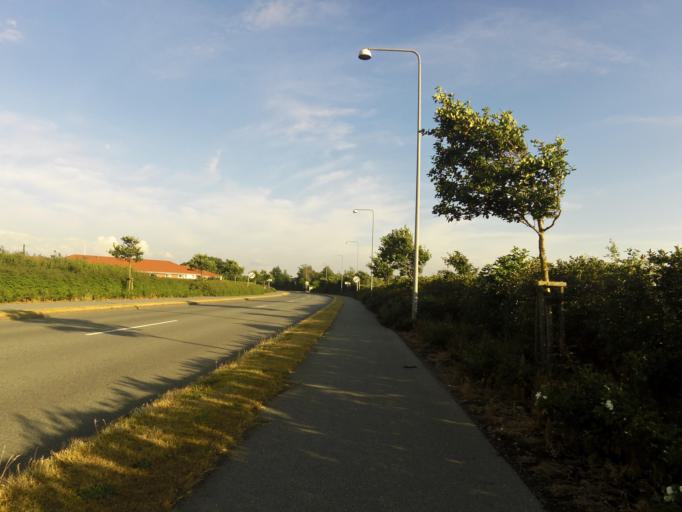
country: DK
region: South Denmark
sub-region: Tonder Kommune
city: Sherrebek
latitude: 55.1630
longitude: 8.7574
